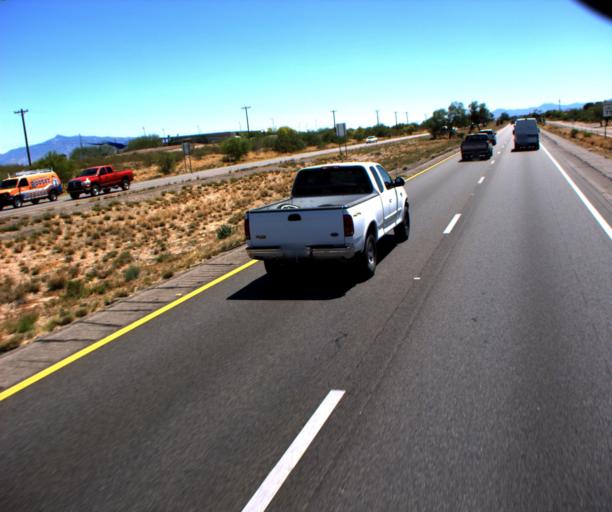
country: US
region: Arizona
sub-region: Pima County
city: Summit
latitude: 32.0971
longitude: -110.8306
